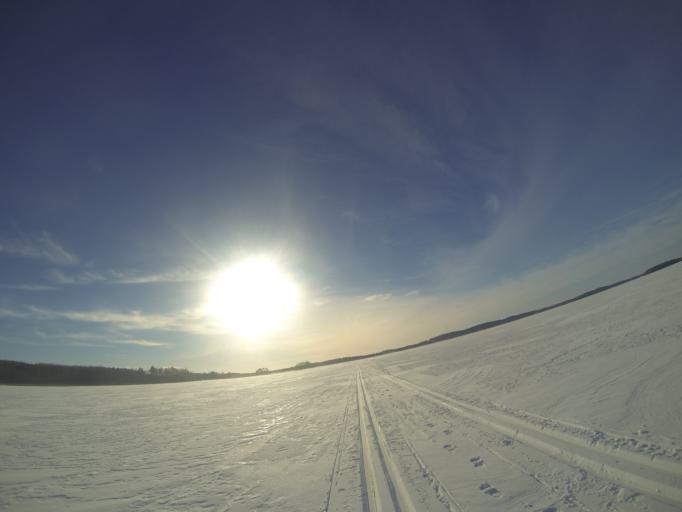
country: FI
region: Southern Savonia
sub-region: Savonlinna
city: Savonlinna
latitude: 61.8938
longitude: 28.9091
